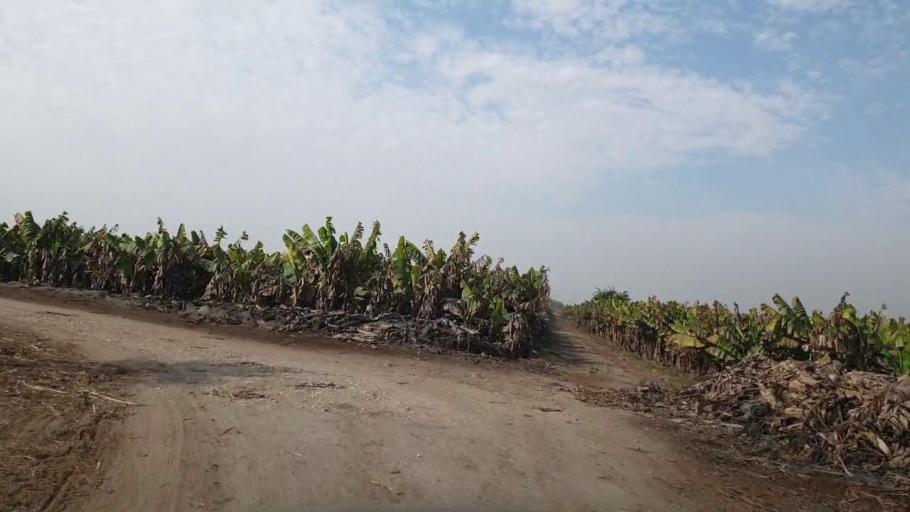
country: PK
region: Sindh
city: Matiari
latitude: 25.5575
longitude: 68.5162
